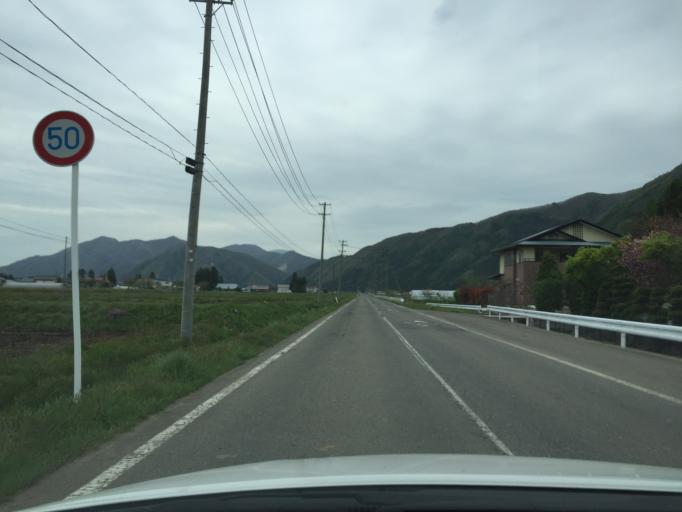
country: JP
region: Fukushima
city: Inawashiro
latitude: 37.5790
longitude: 140.1370
